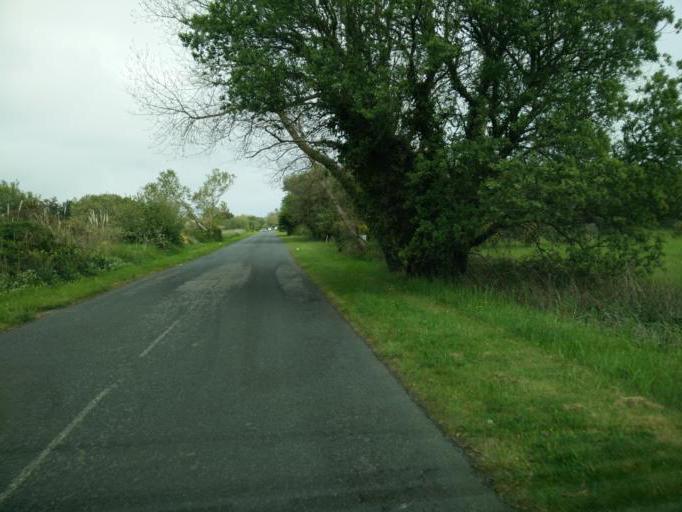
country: FR
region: Brittany
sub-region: Departement du Finistere
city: Plobannalec-Lesconil
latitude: 47.8036
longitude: -4.2013
